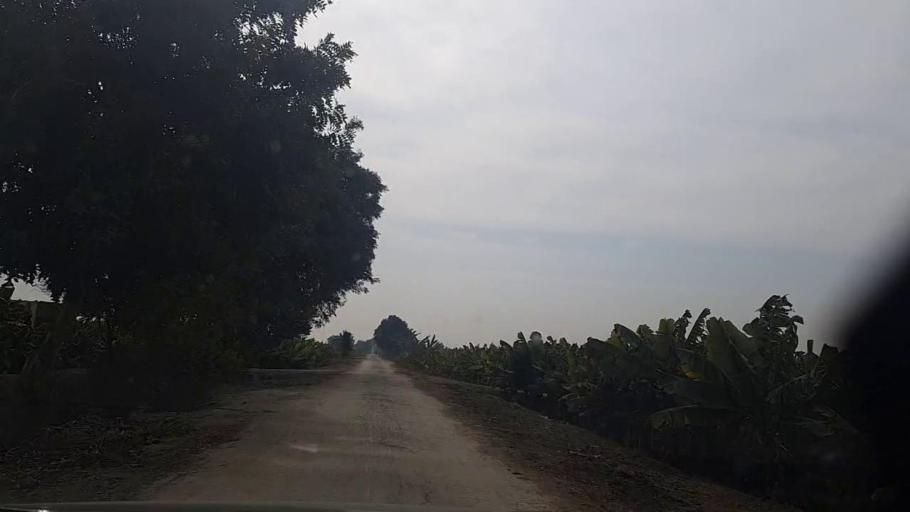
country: PK
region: Sindh
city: Sakrand
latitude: 26.2355
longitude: 68.2971
